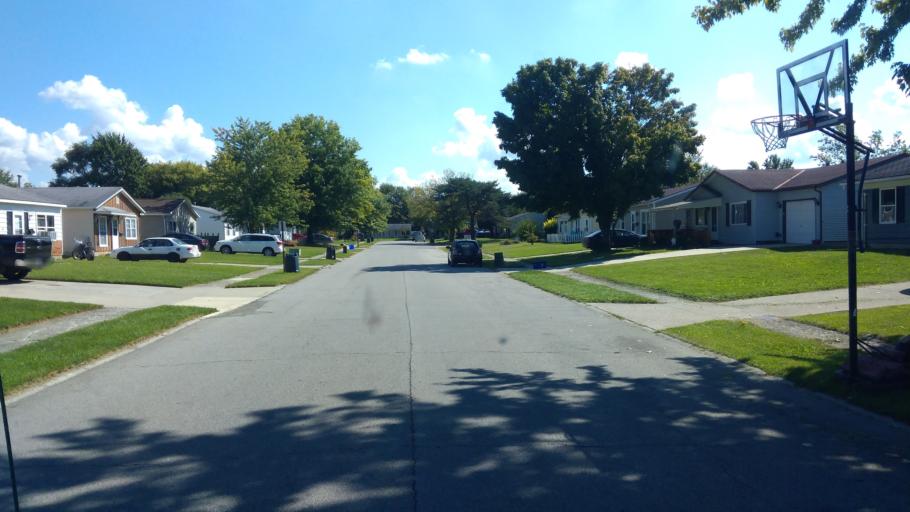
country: US
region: Ohio
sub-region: Marion County
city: Marion
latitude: 40.6108
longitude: -83.1148
